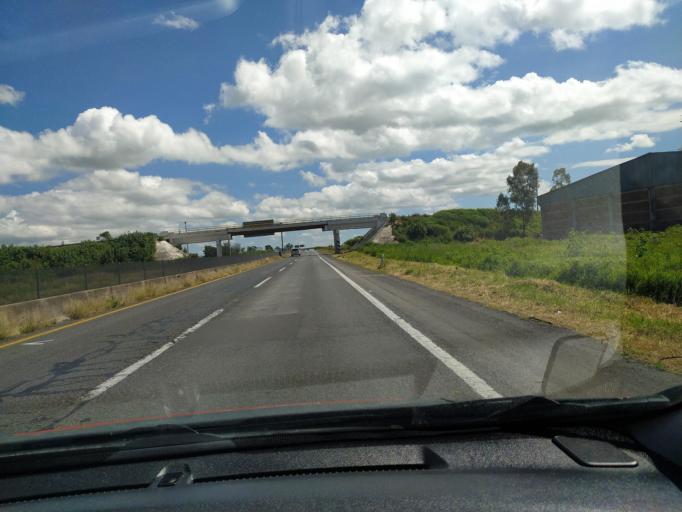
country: MX
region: Jalisco
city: Tepatitlan de Morelos
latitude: 20.8906
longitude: -102.7135
